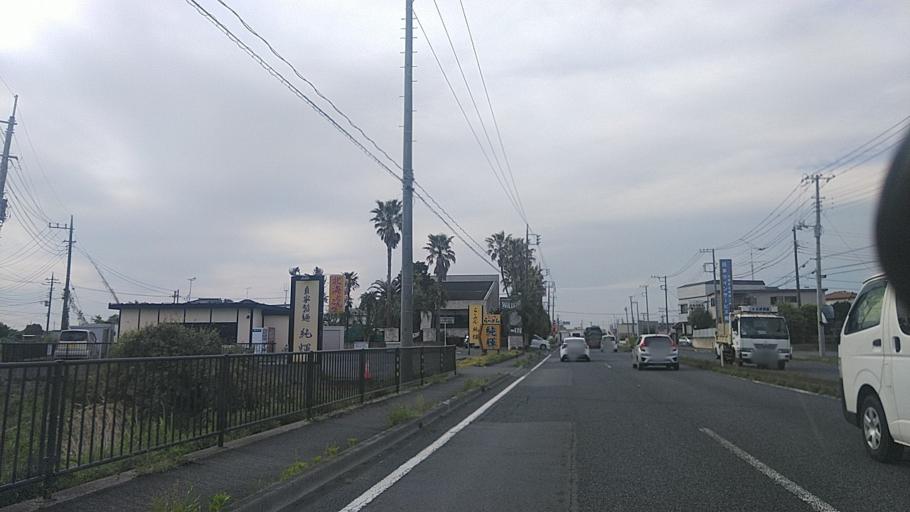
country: JP
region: Chiba
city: Shiroi
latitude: 35.7501
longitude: 140.1164
